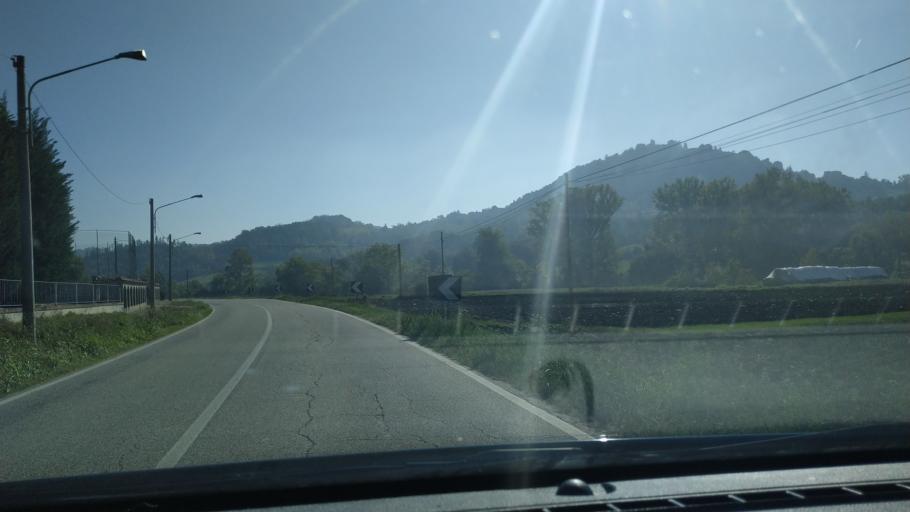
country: IT
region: Piedmont
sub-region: Provincia di Alessandria
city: Villadeati
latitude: 45.0808
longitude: 8.1577
